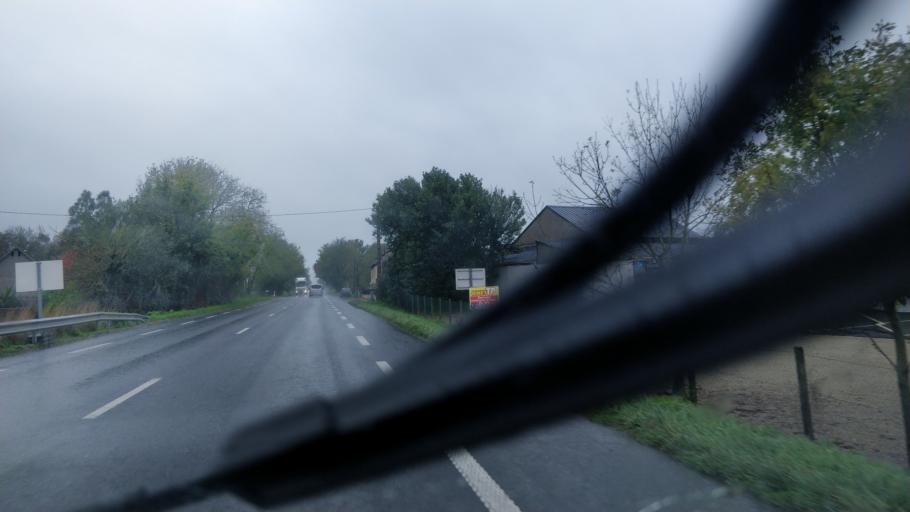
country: FR
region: Lower Normandy
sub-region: Departement de la Manche
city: Brehal
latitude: 48.8756
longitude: -1.5345
